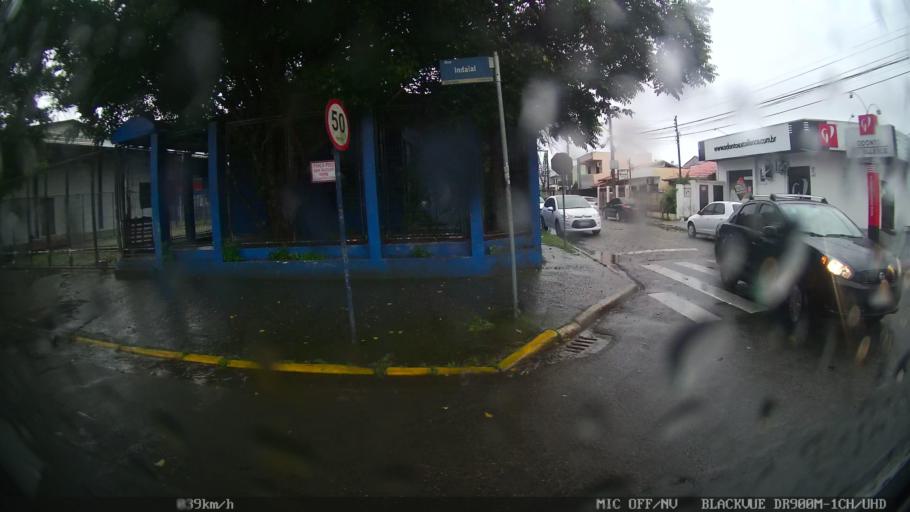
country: BR
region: Santa Catarina
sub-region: Itajai
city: Itajai
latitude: -26.9039
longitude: -48.6777
